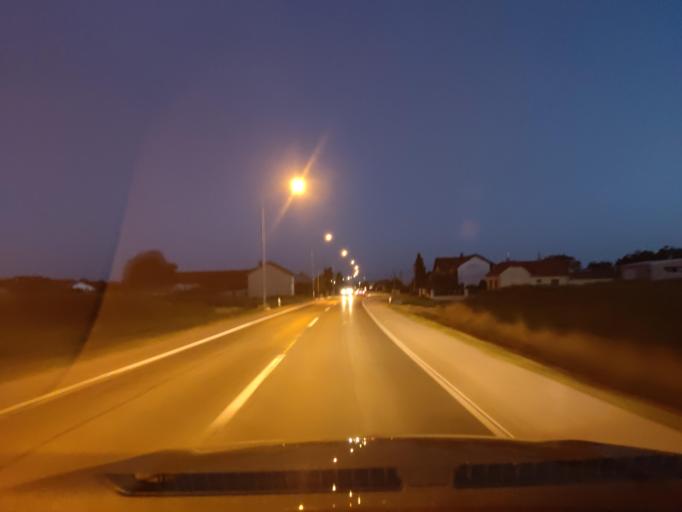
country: HR
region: Medimurska
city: Senkovec
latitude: 46.4166
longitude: 16.4247
